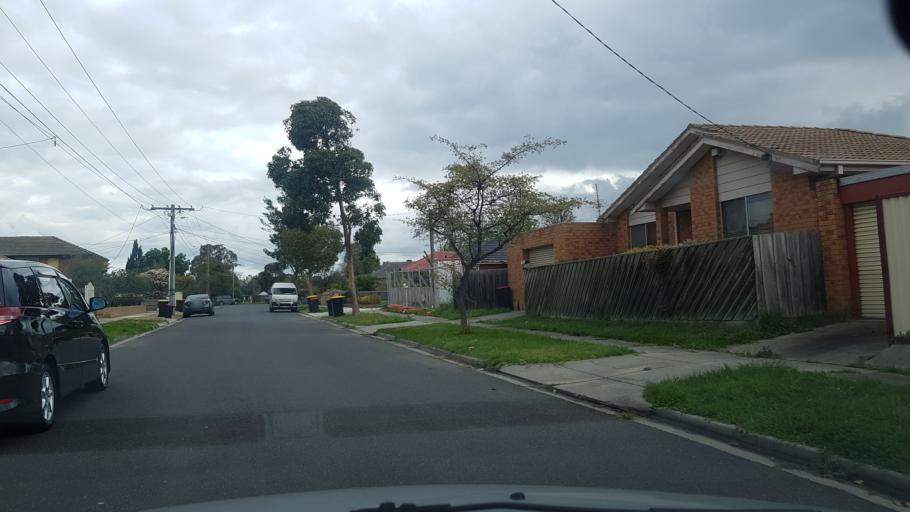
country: AU
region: Victoria
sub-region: Greater Dandenong
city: Springvale
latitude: -37.9373
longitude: 145.1472
